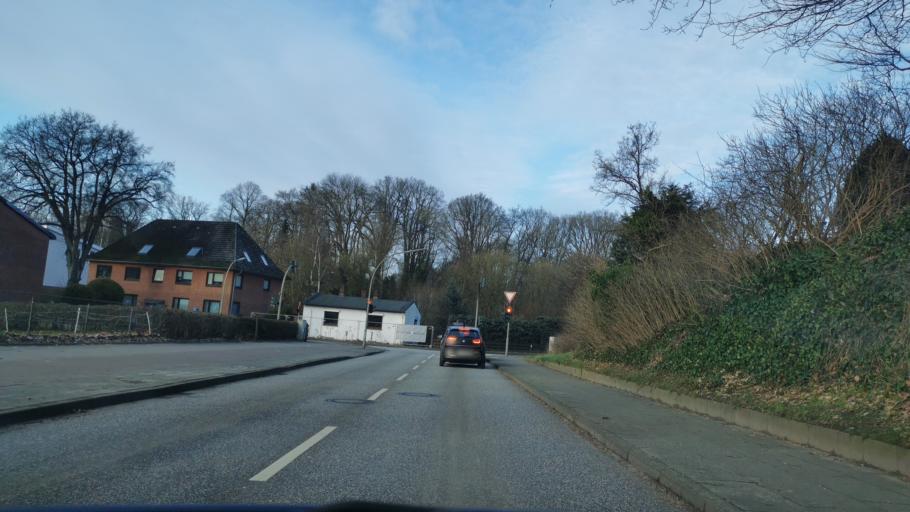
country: DE
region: Hamburg
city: Harburg
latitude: 53.4354
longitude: 9.9688
